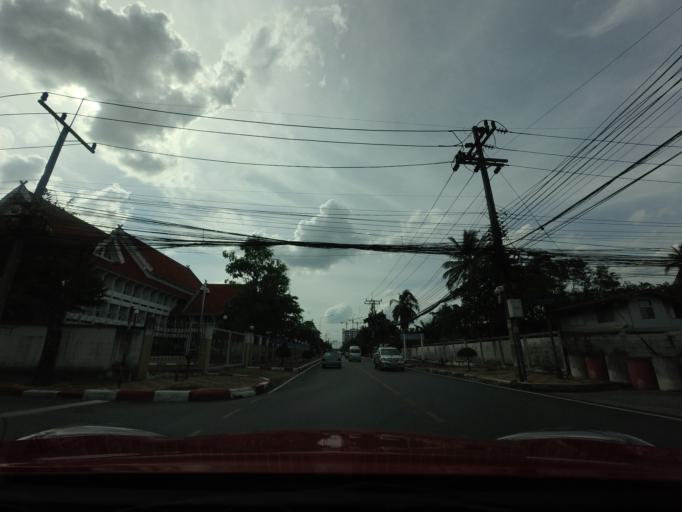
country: TH
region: Yala
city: Yala
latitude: 6.5430
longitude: 101.2790
